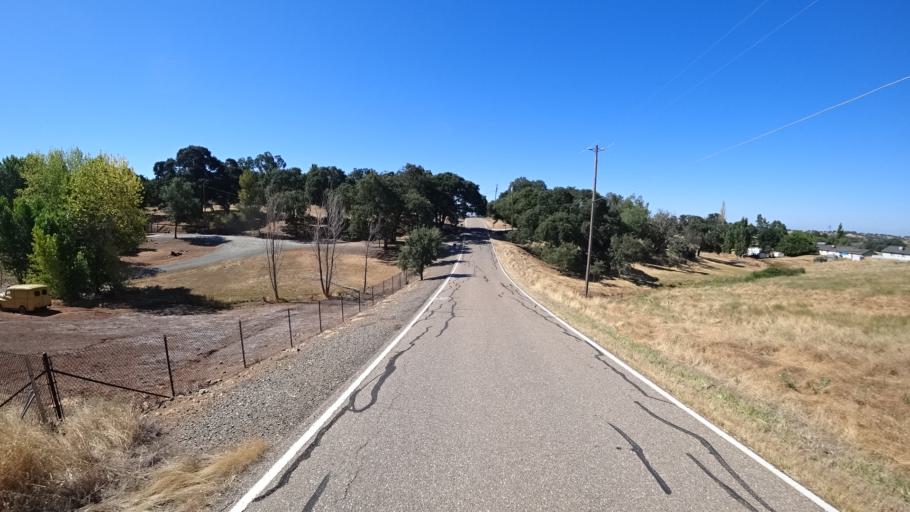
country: US
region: California
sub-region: Calaveras County
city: Rancho Calaveras
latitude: 38.1026
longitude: -120.8673
